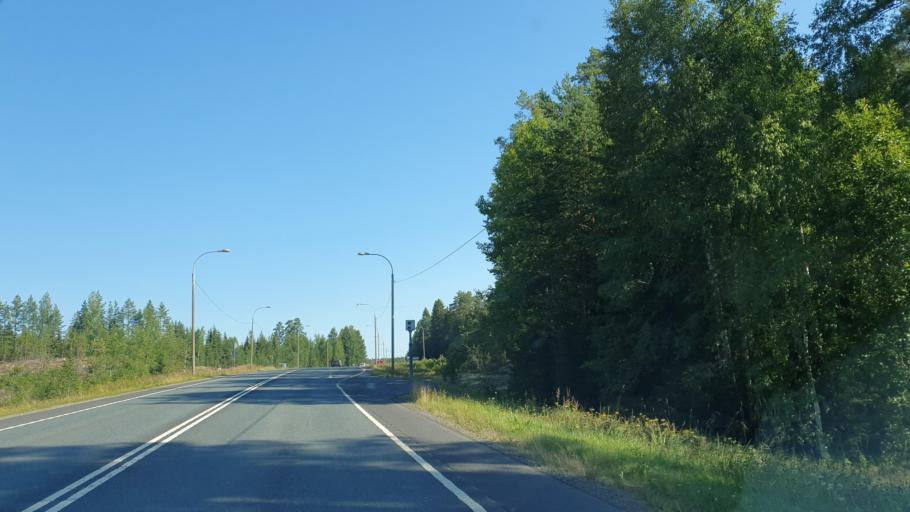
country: FI
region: Northern Savo
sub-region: Sisae-Savo
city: Suonenjoki
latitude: 62.6130
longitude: 27.0720
